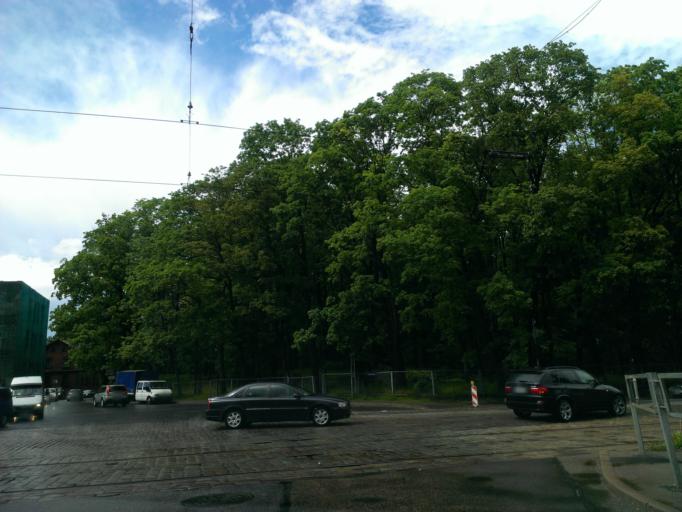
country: LV
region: Riga
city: Riga
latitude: 56.9273
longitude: 24.0911
